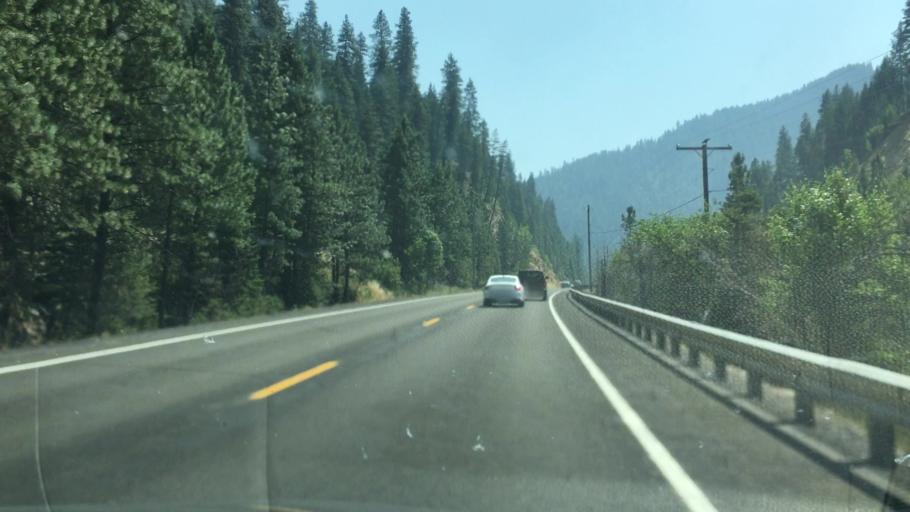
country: US
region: Idaho
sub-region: Valley County
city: McCall
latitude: 45.1600
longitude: -116.2994
